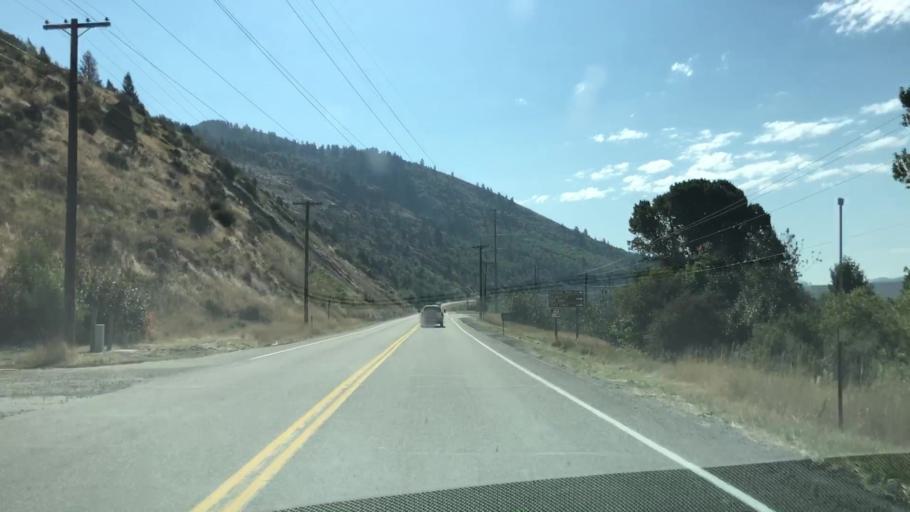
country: US
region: Idaho
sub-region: Teton County
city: Victor
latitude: 43.3465
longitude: -111.2093
